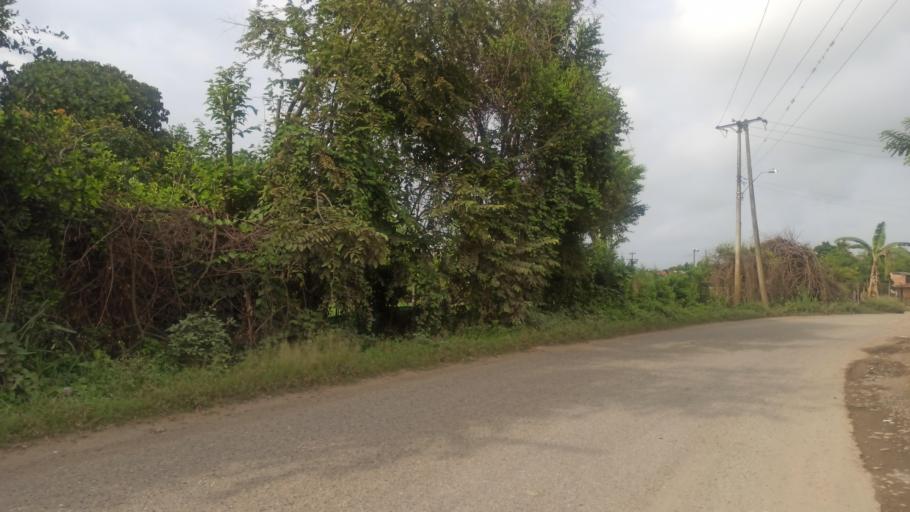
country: CO
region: Valle del Cauca
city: Jamundi
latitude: 3.2012
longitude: -76.5015
